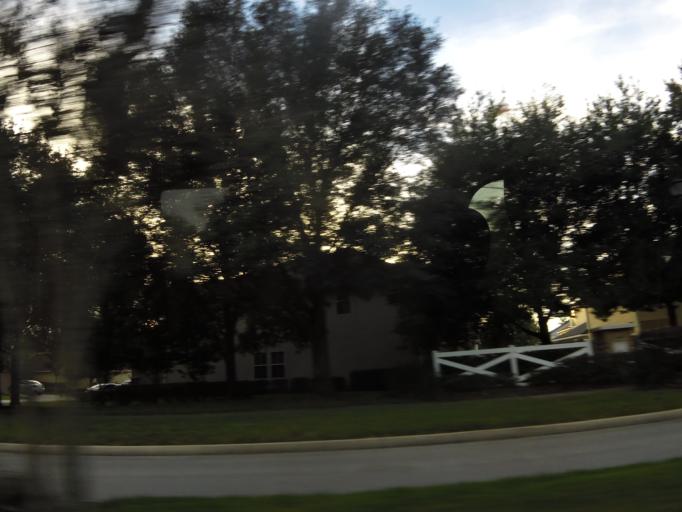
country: US
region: Florida
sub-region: Saint Johns County
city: Fruit Cove
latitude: 30.1591
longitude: -81.5483
